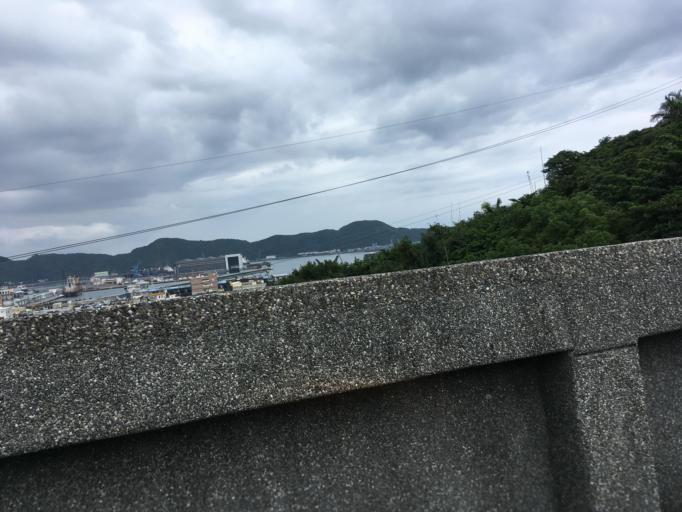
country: TW
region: Taiwan
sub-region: Yilan
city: Yilan
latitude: 24.5790
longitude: 121.8679
